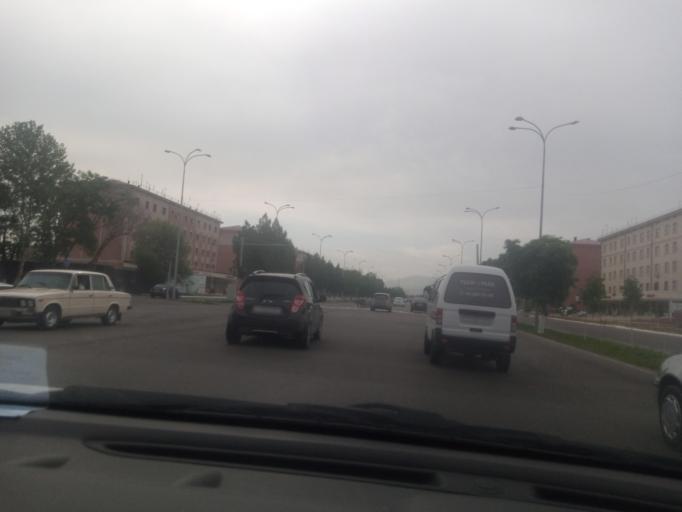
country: UZ
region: Toshkent
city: Ohangaron
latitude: 40.9089
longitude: 69.6247
